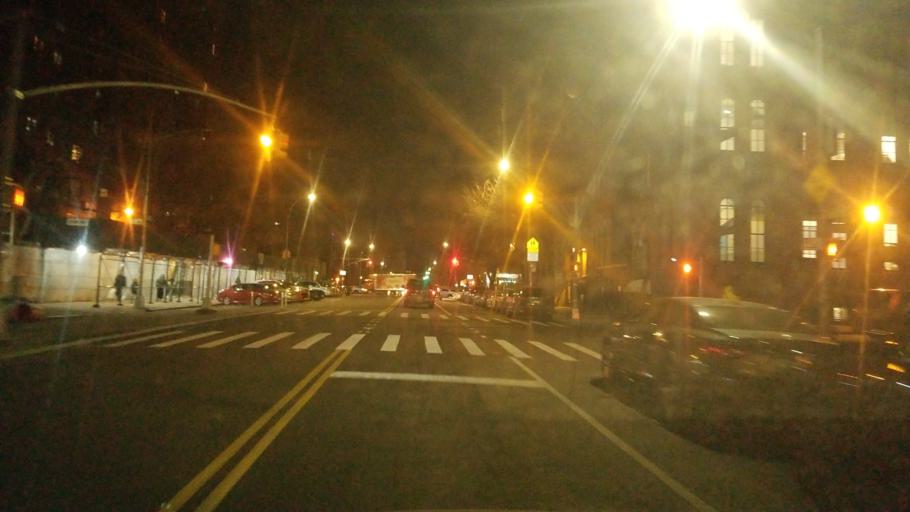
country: US
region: New York
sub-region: New York County
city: Manhattan
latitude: 40.8092
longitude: -73.9258
